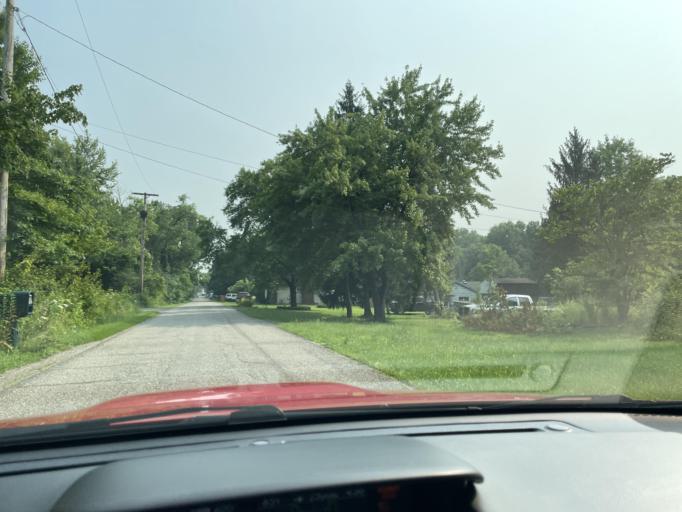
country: US
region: Ohio
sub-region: Trumbull County
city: McDonald
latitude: 41.1611
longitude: -80.7365
